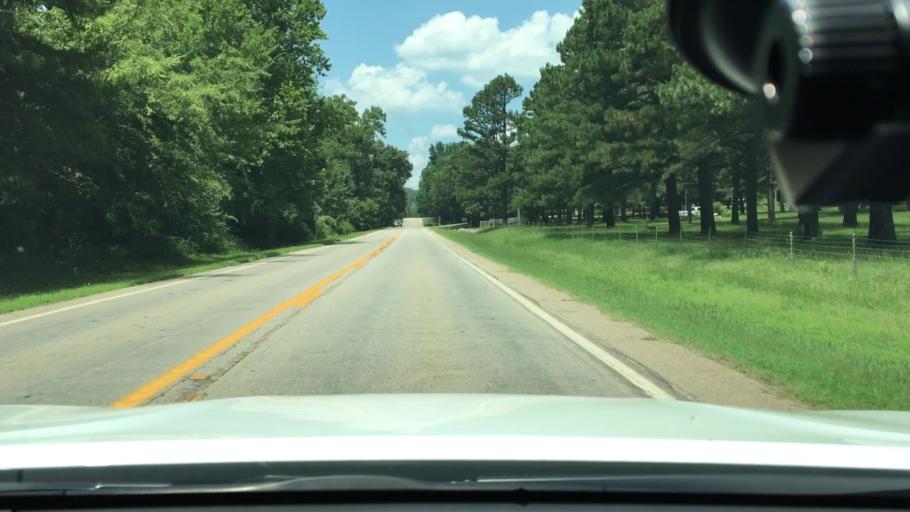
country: US
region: Arkansas
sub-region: Logan County
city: Booneville
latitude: 35.2107
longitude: -93.9279
